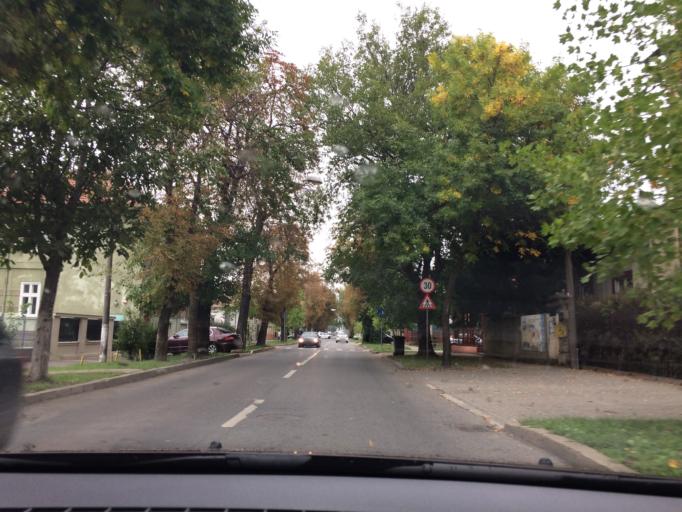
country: RO
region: Timis
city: Timisoara
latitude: 45.7553
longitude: 21.2094
